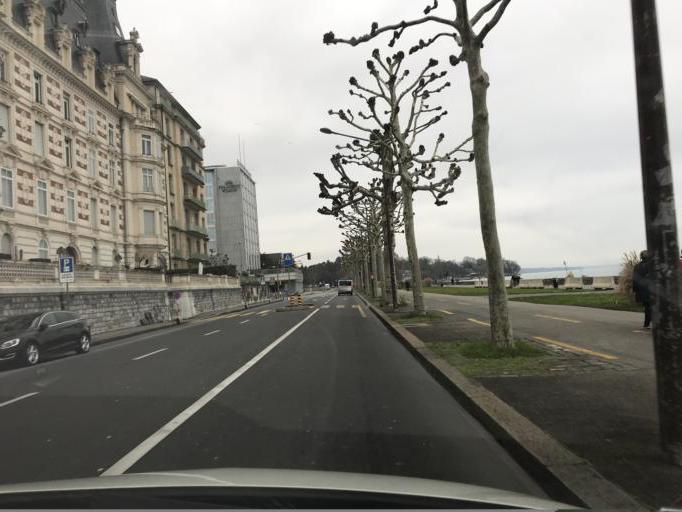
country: CH
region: Geneva
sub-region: Geneva
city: Geneve
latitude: 46.2131
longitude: 6.1524
